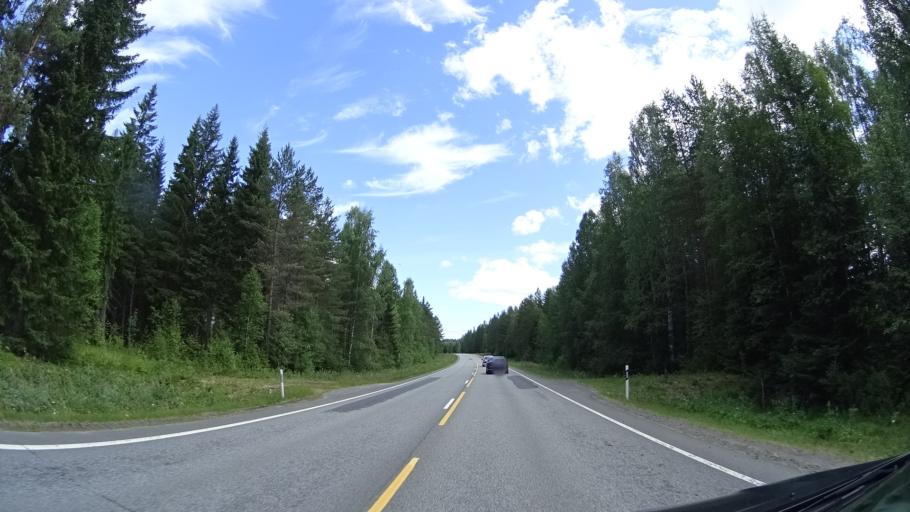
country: FI
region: Pirkanmaa
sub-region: Luoteis-Pirkanmaa
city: Kihnioe
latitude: 62.1358
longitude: 23.1415
